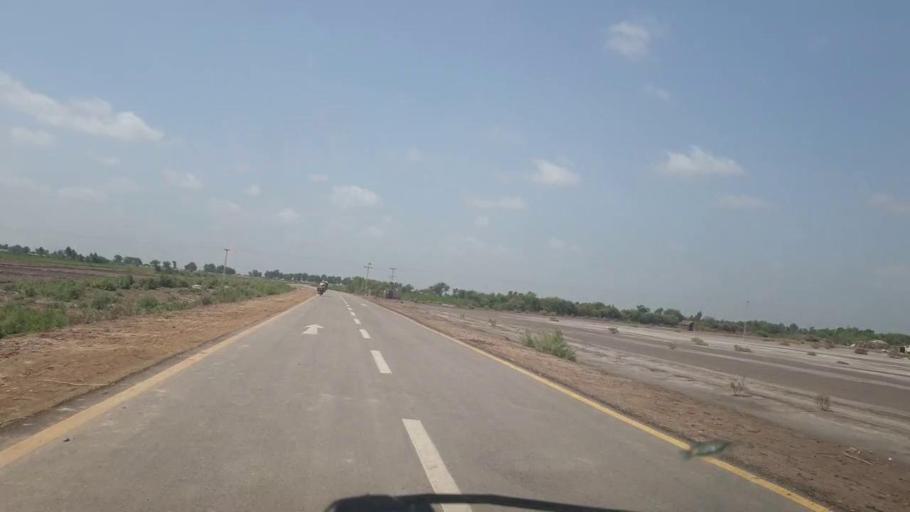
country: PK
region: Sindh
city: Berani
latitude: 25.7106
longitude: 68.9430
